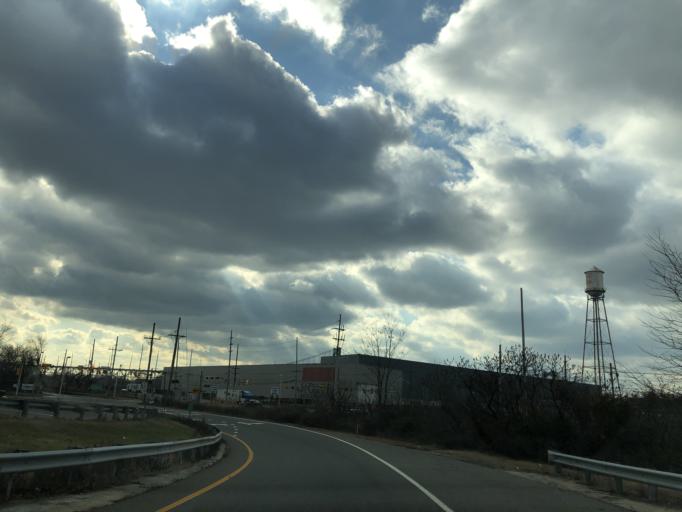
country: US
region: New Jersey
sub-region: Camden County
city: Camden
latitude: 39.9139
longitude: -75.1170
